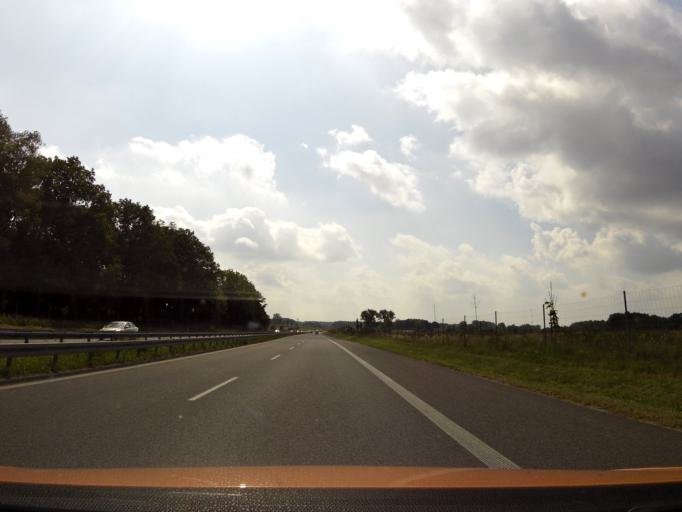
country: PL
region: West Pomeranian Voivodeship
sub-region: Powiat goleniowski
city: Nowogard
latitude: 53.6641
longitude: 15.0758
